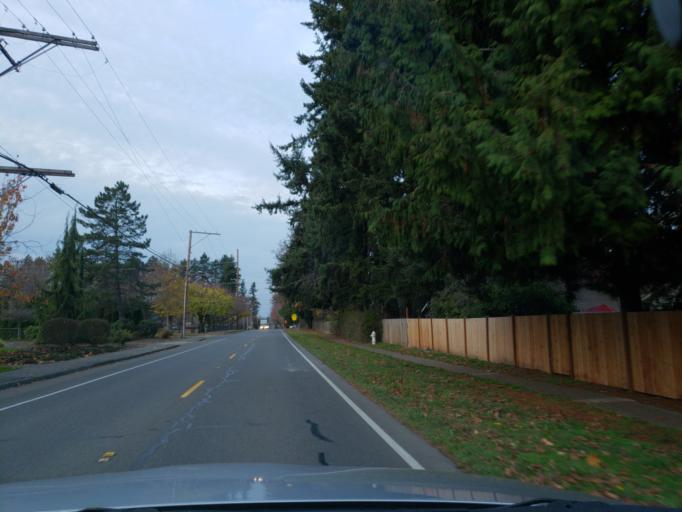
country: US
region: Washington
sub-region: King County
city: Bothell
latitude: 47.7683
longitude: -122.2232
